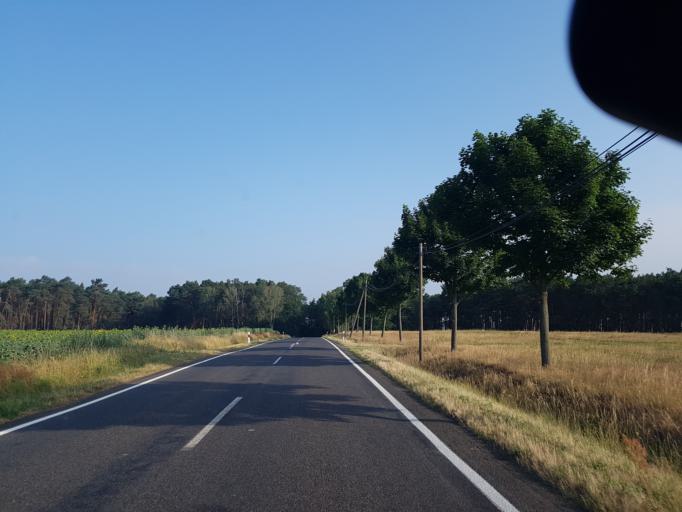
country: DE
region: Brandenburg
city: Ihlow
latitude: 51.8110
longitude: 13.2912
